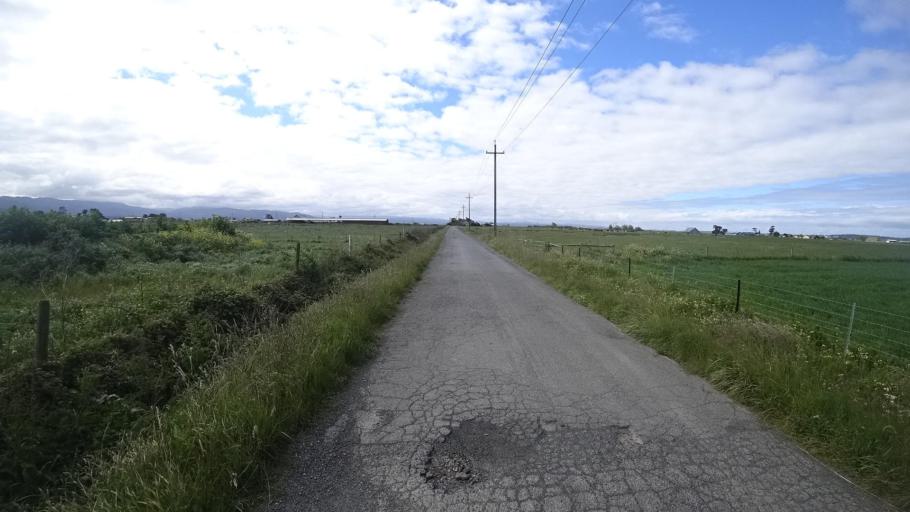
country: US
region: California
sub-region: Humboldt County
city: Arcata
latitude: 40.8869
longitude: -124.1156
